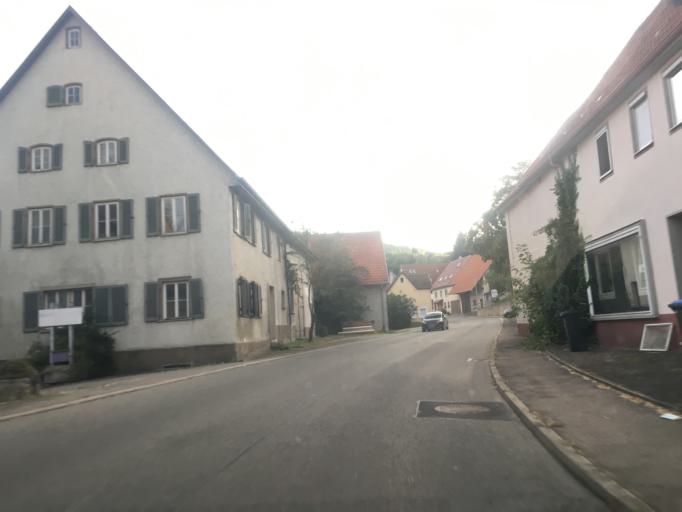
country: DE
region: Baden-Wuerttemberg
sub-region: Tuebingen Region
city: Gomadingen
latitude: 48.3751
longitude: 9.4247
